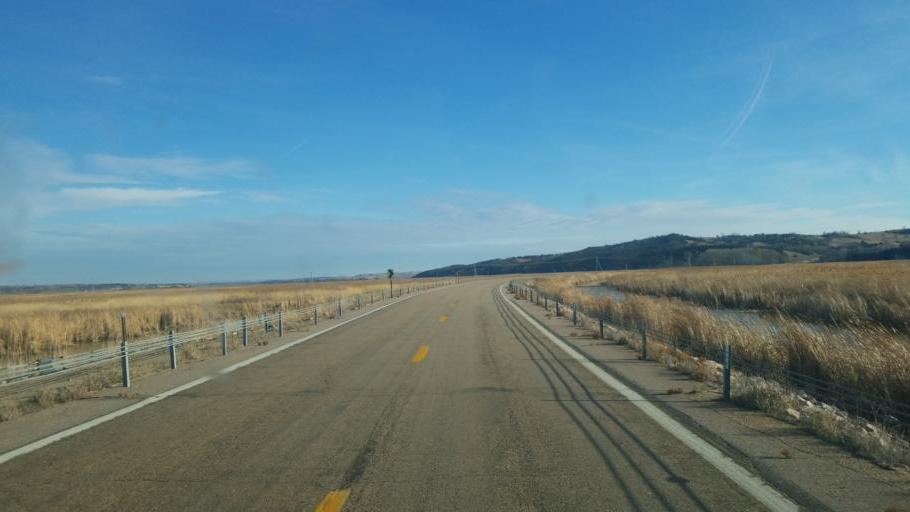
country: US
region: South Dakota
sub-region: Bon Homme County
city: Springfield
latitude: 42.7838
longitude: -98.0936
